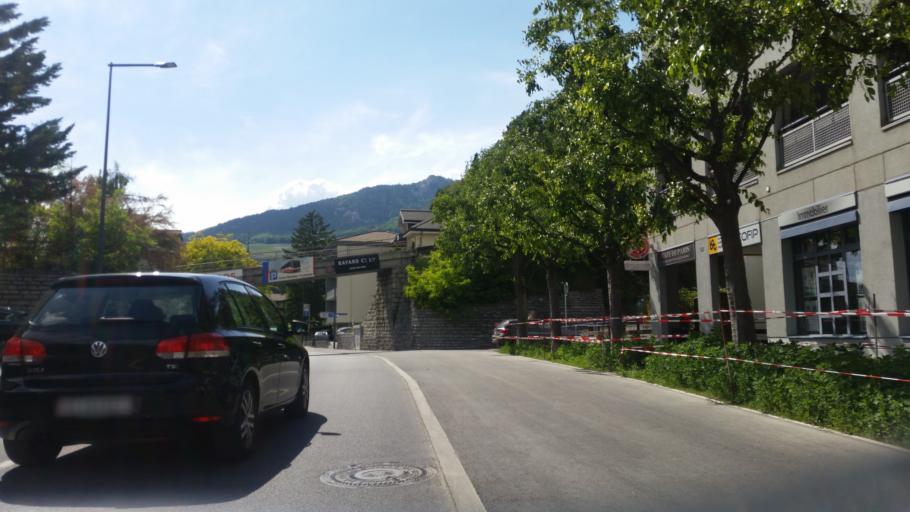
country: CH
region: Valais
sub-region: Sierre District
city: Sierre
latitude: 46.2934
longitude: 7.5304
